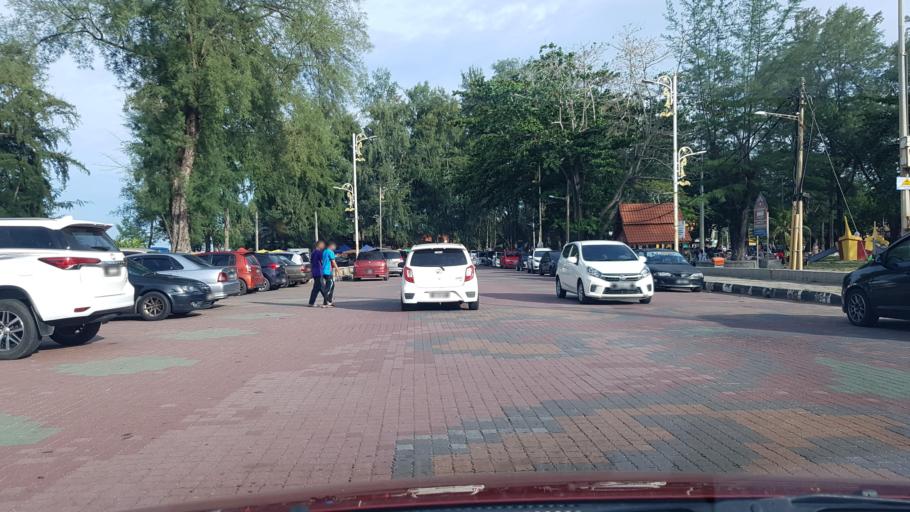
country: MY
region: Terengganu
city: Kuala Terengganu
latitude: 5.3225
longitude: 103.1546
